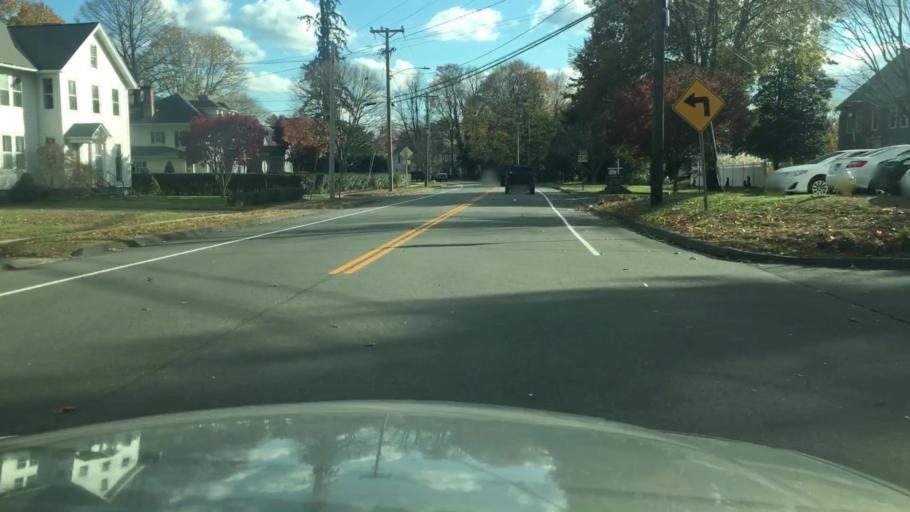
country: US
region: Connecticut
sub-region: Middlesex County
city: Old Saybrook
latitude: 41.2865
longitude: -72.3754
